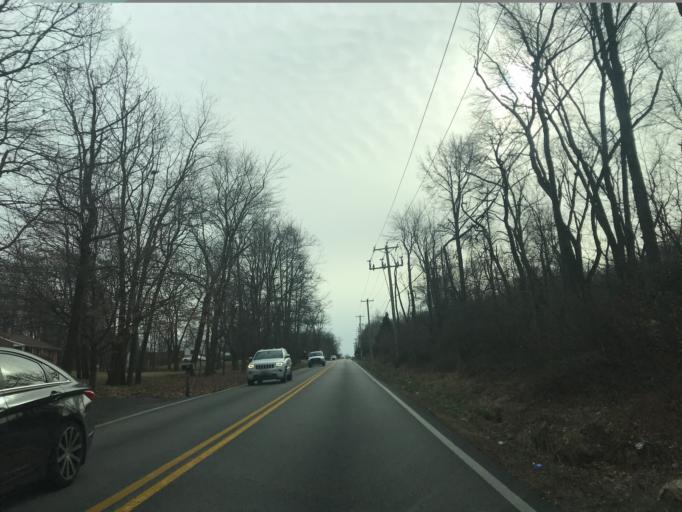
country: US
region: Maryland
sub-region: Cecil County
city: Elkton
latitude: 39.6186
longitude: -75.7920
